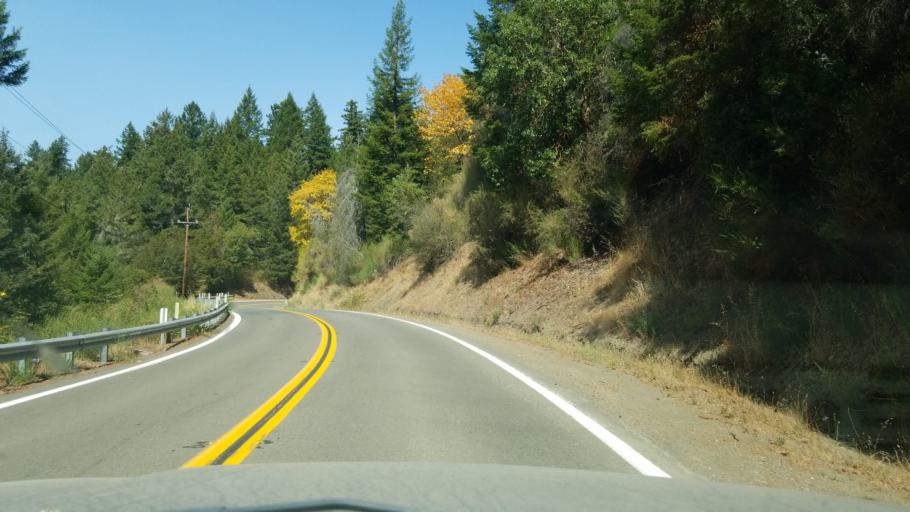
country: US
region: California
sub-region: Mendocino County
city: Laytonville
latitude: 39.8523
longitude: -123.7182
